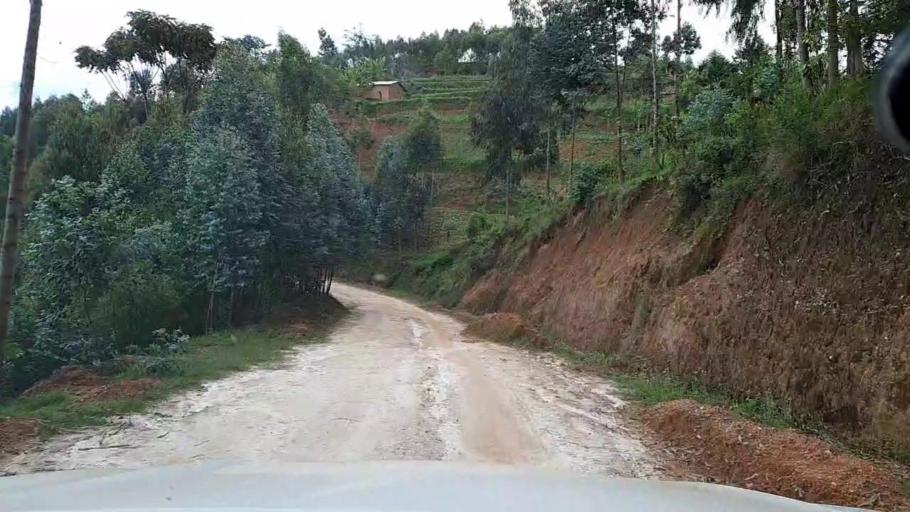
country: RW
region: Southern Province
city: Nzega
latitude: -2.6967
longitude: 29.4409
